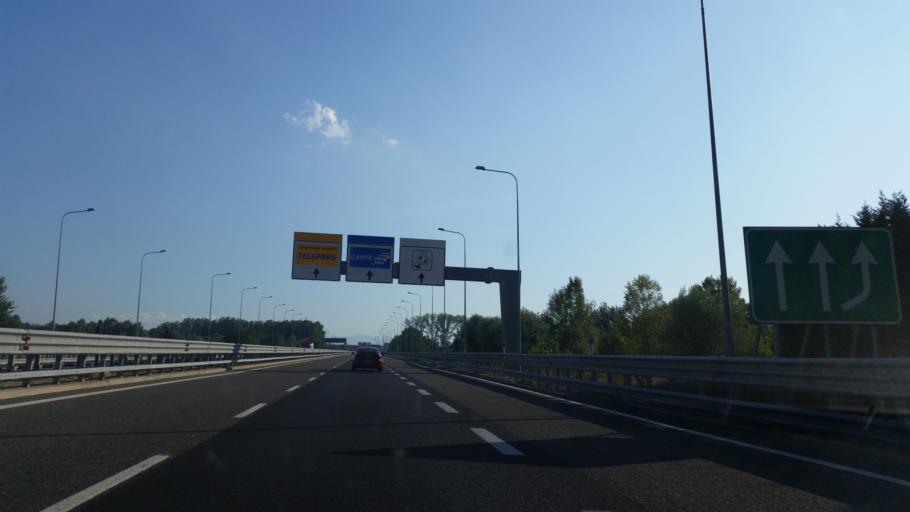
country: IT
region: Piedmont
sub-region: Provincia di Cuneo
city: Govone
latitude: 44.7746
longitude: 8.1070
